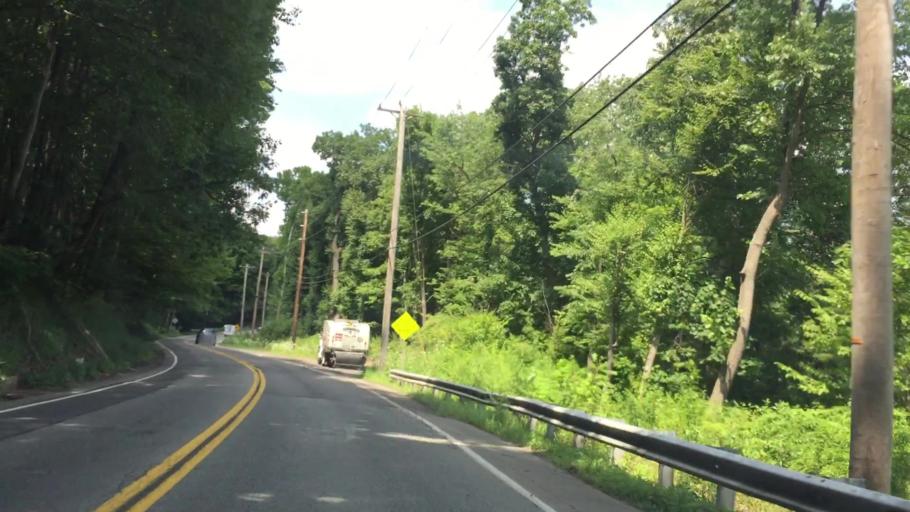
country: US
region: Pennsylvania
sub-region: Allegheny County
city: Allison Park
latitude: 40.5666
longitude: -79.9809
